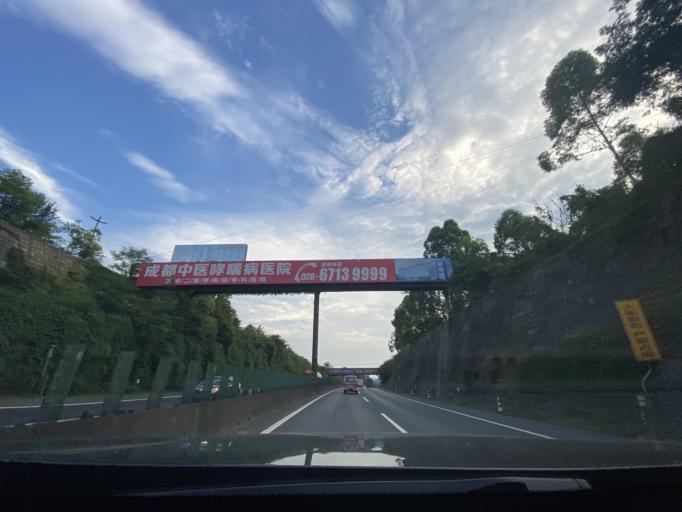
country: CN
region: Sichuan
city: Luojiang
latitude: 31.4059
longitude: 104.5739
